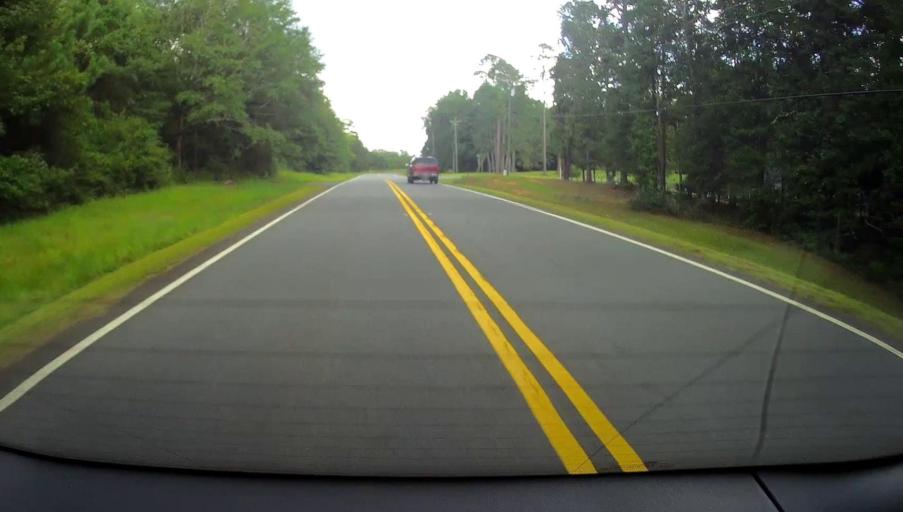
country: US
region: Georgia
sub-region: Monroe County
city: Forsyth
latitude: 32.8818
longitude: -83.9326
